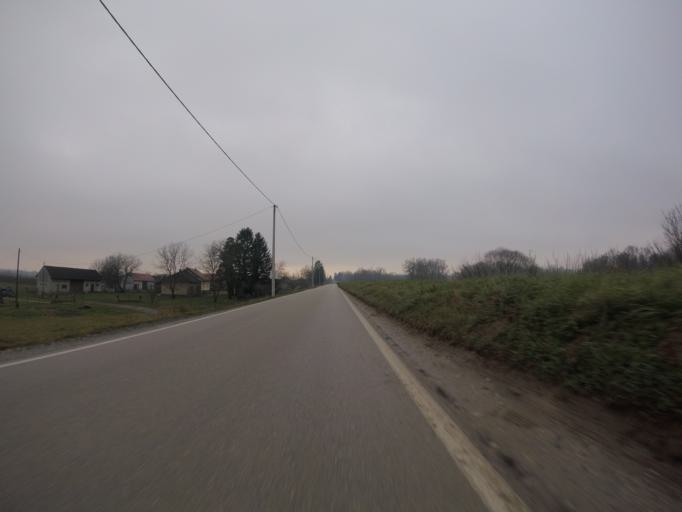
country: HR
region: Zagrebacka
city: Kuce
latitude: 45.6931
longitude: 16.2273
